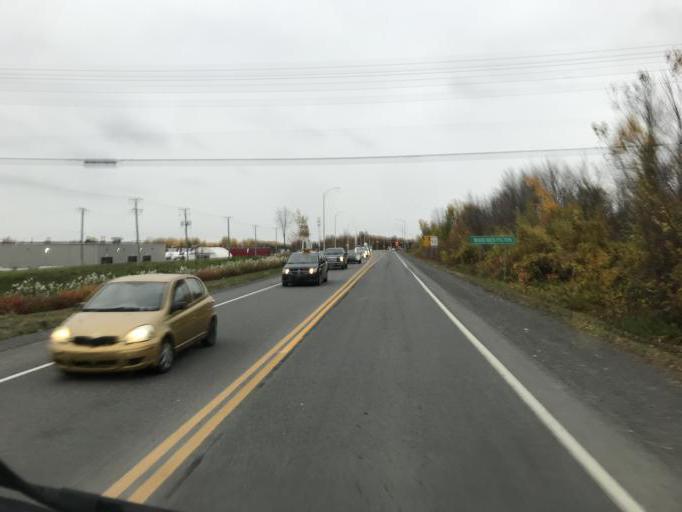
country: CA
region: Quebec
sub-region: Lanaudiere
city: Lorraine
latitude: 45.6824
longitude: -73.7733
